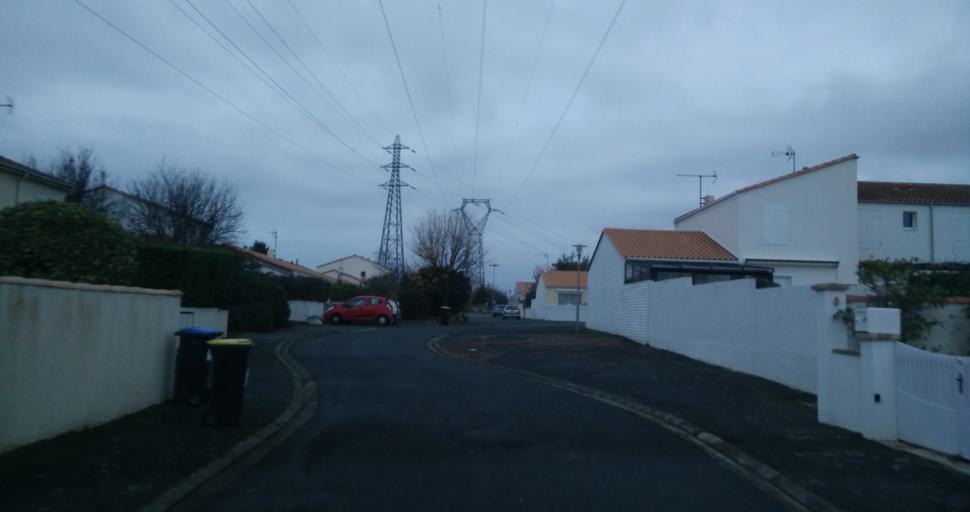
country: FR
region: Poitou-Charentes
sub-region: Departement de la Charente-Maritime
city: Puilboreau
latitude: 46.1827
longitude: -1.1229
